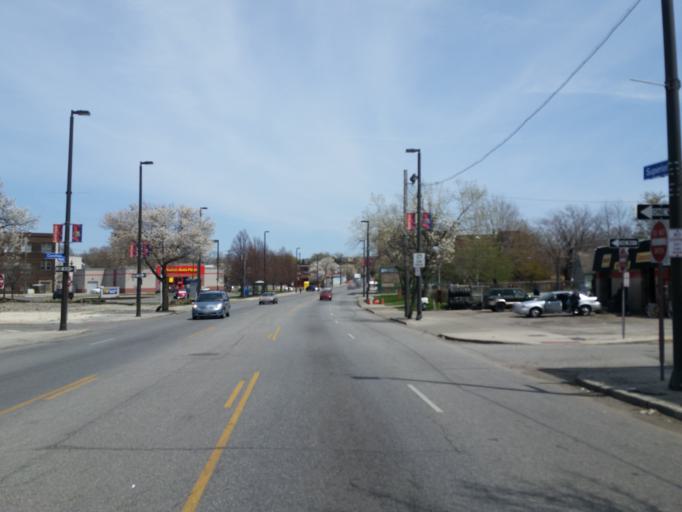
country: US
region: Ohio
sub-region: Cuyahoga County
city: East Cleveland
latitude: 41.5229
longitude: -81.6039
